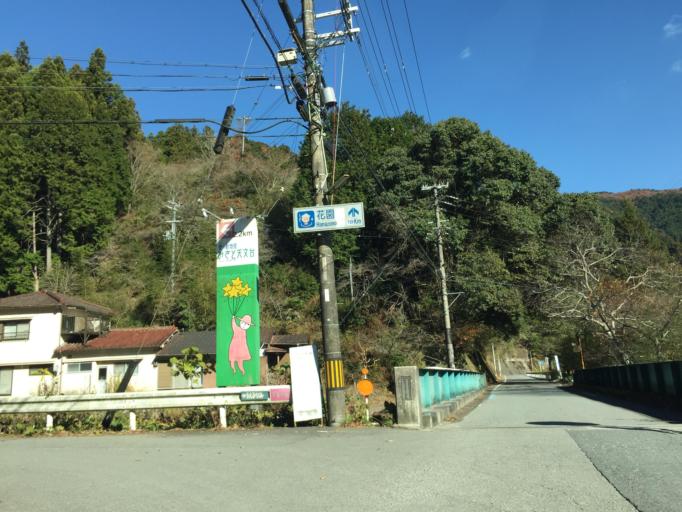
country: JP
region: Wakayama
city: Iwade
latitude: 34.1414
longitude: 135.4180
